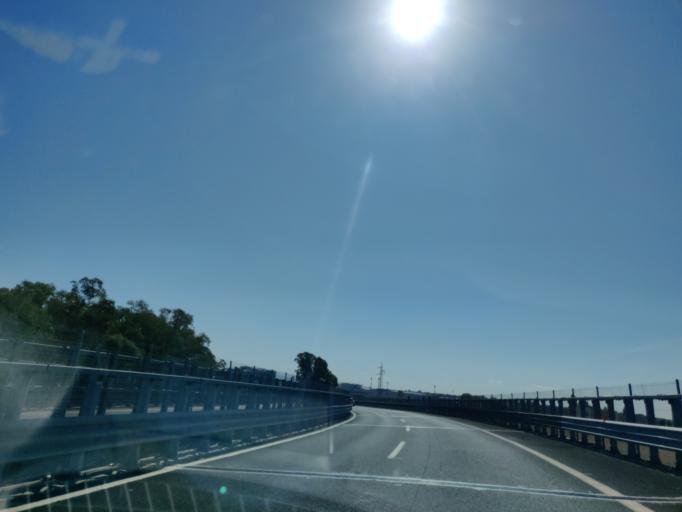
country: IT
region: Latium
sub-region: Citta metropolitana di Roma Capitale
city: Npp 23 (Parco Leonardo)
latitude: 41.8096
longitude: 12.3099
